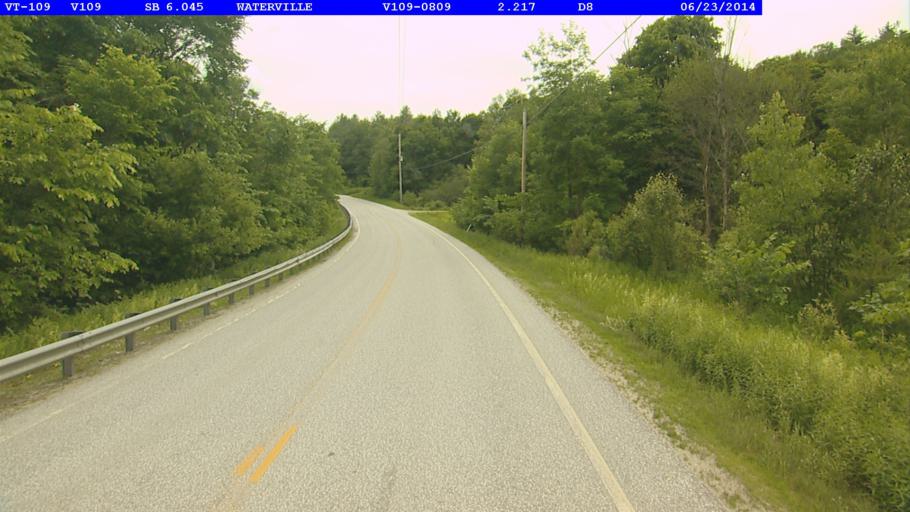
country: US
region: Vermont
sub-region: Lamoille County
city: Johnson
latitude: 44.7117
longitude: -72.7587
